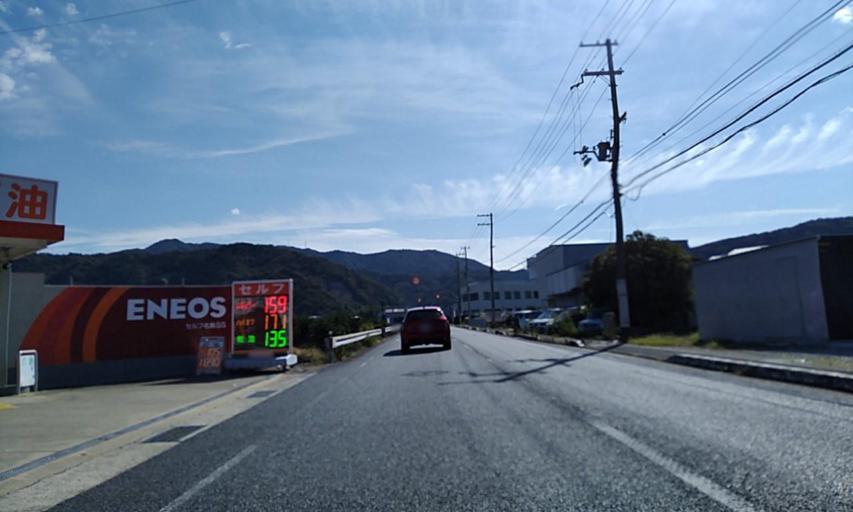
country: JP
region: Wakayama
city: Kainan
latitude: 34.0196
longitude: 135.1813
